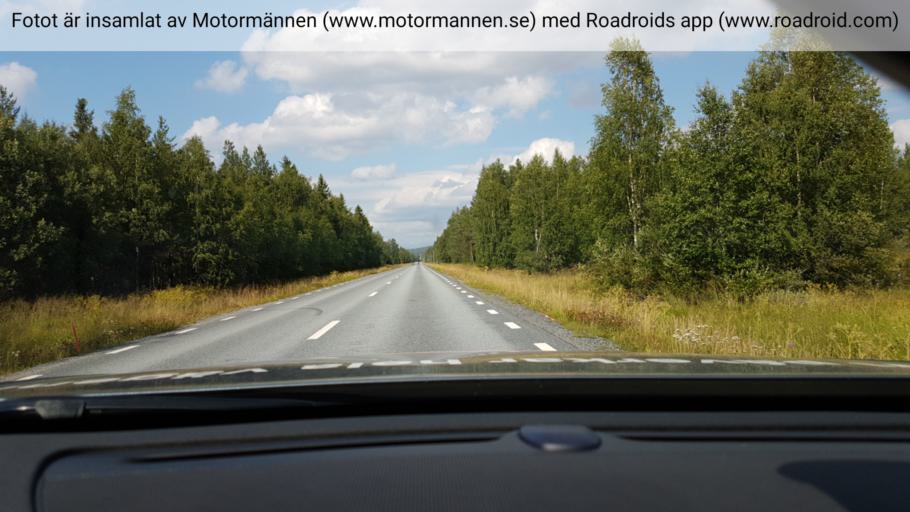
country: SE
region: Vaesterbotten
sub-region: Sorsele Kommun
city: Sorsele
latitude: 65.5175
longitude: 17.5397
